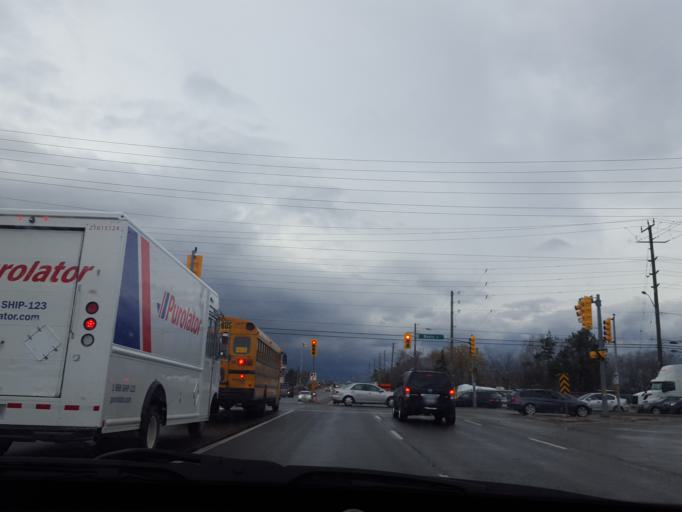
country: CA
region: Ontario
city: Ajax
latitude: 43.8326
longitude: -79.0675
